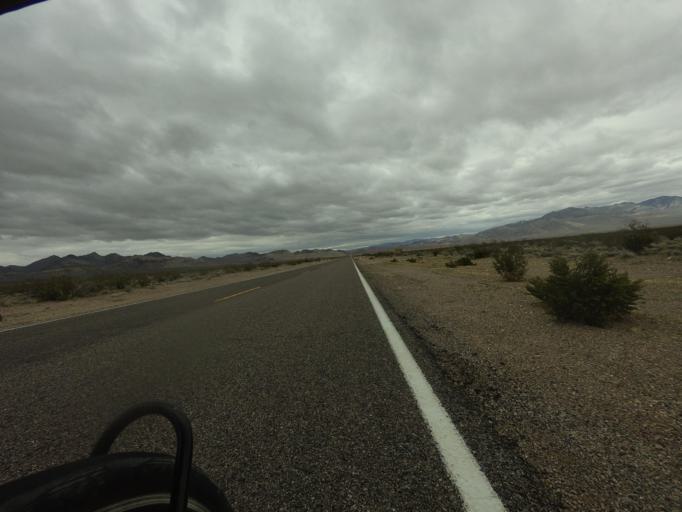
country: US
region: Nevada
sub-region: Nye County
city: Beatty
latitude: 36.8529
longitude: -116.8538
